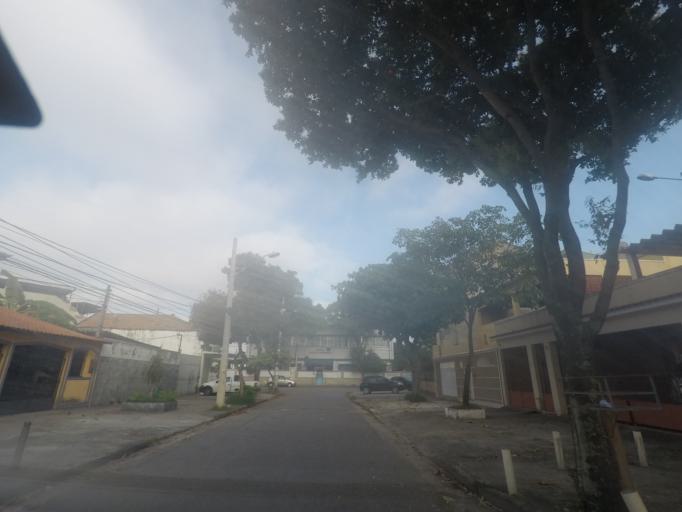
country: BR
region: Rio de Janeiro
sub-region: Duque De Caxias
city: Duque de Caxias
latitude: -22.8344
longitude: -43.2707
